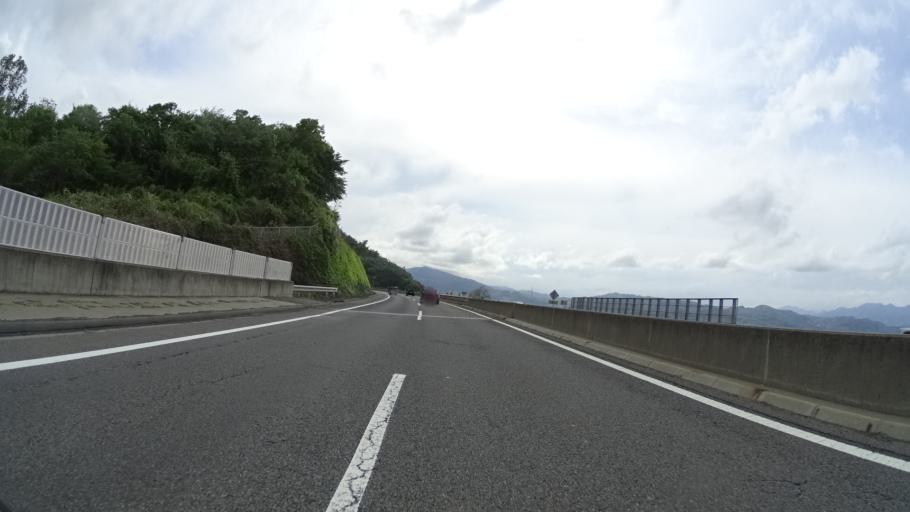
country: JP
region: Nagano
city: Nagano-shi
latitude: 36.5638
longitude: 138.1742
